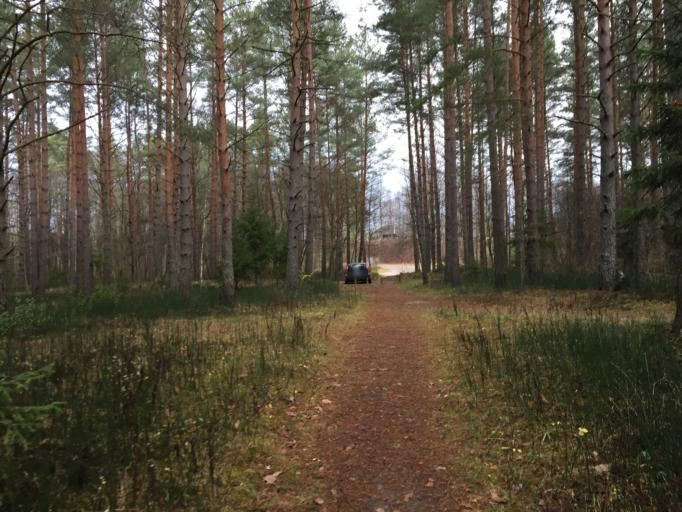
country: LV
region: Valmieras Rajons
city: Valmiera
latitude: 57.5422
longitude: 25.4567
